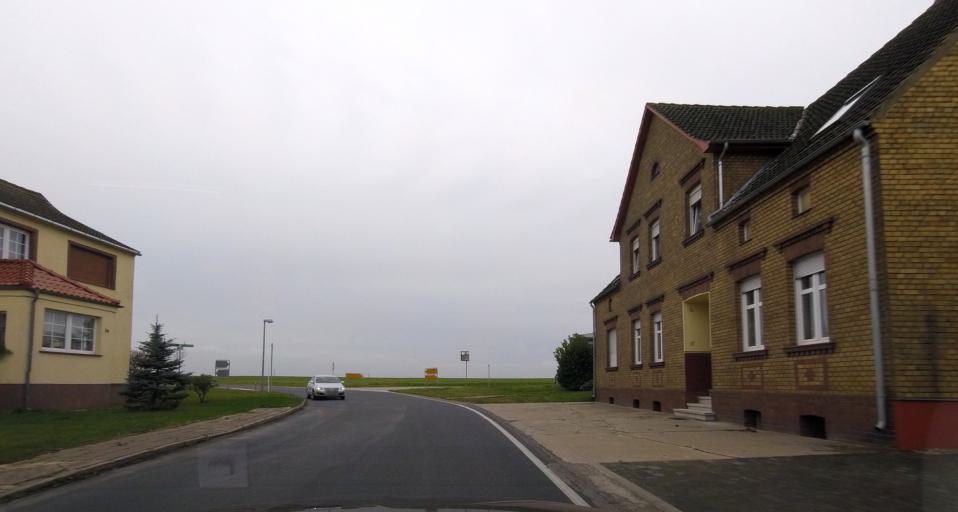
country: DE
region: Saxony-Anhalt
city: Kropstadt
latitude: 52.0234
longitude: 12.7404
